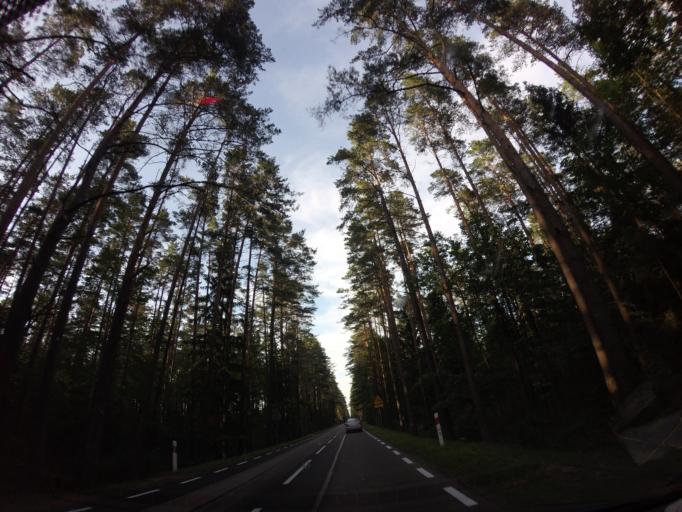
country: PL
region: Podlasie
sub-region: Powiat augustowski
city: Augustow
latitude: 53.8712
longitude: 23.0972
